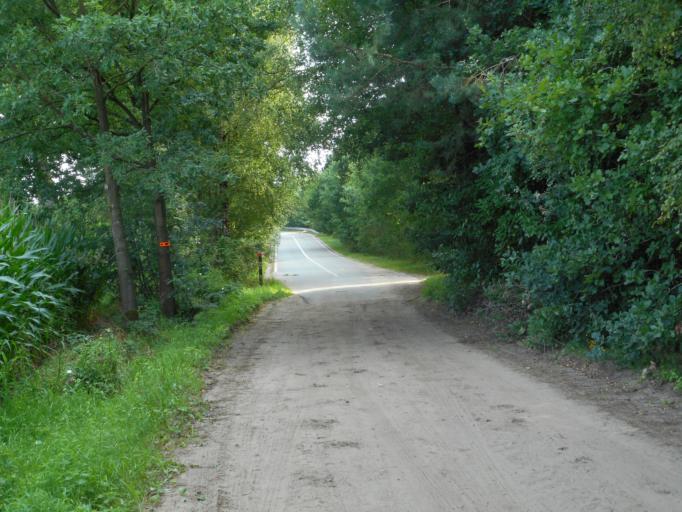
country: BE
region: Flanders
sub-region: Provincie Antwerpen
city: Lille
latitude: 51.2669
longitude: 4.8178
